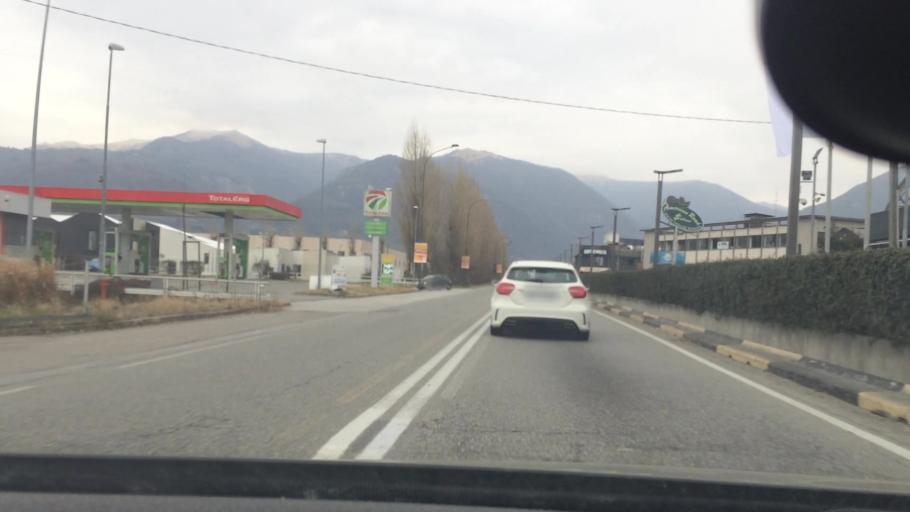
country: IT
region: Lombardy
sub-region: Provincia di Como
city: Merone
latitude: 45.7987
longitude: 9.2392
